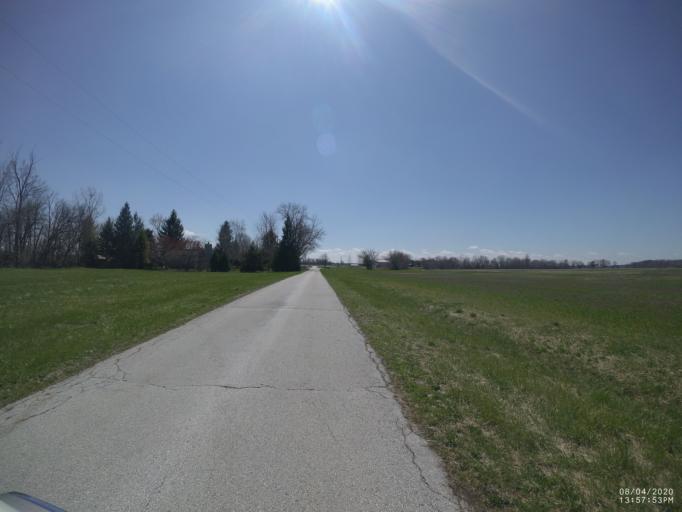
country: US
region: Ohio
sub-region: Sandusky County
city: Gibsonburg
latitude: 41.2999
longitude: -83.2864
